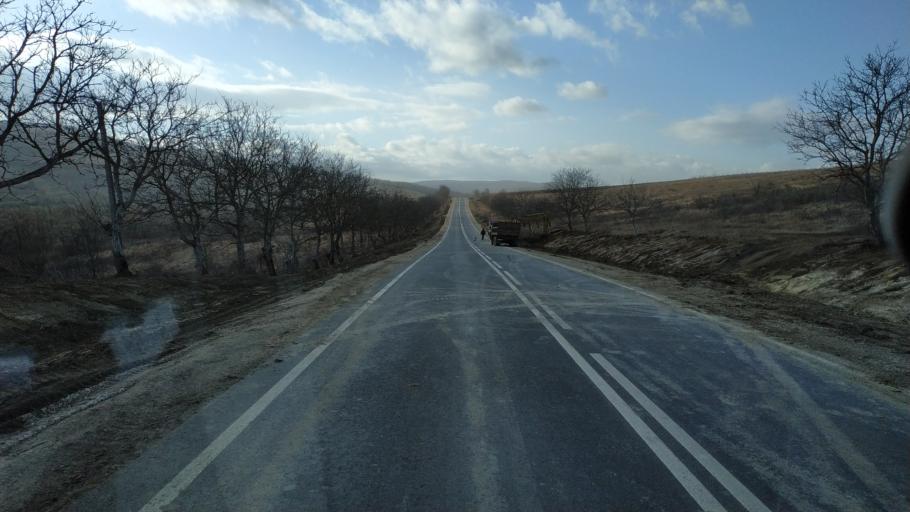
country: MD
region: Calarasi
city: Calarasi
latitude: 47.2959
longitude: 28.1605
